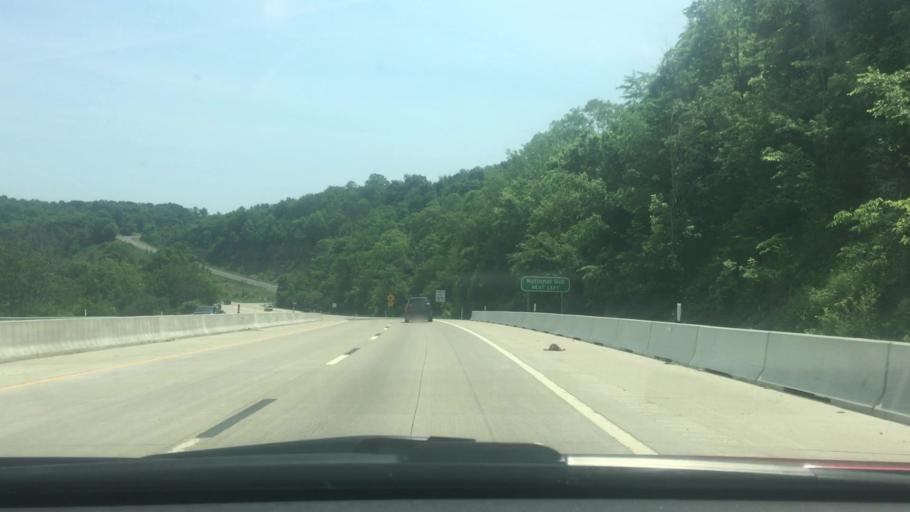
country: US
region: Pennsylvania
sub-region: Washington County
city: Cecil-Bishop
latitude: 40.3451
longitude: -80.1593
